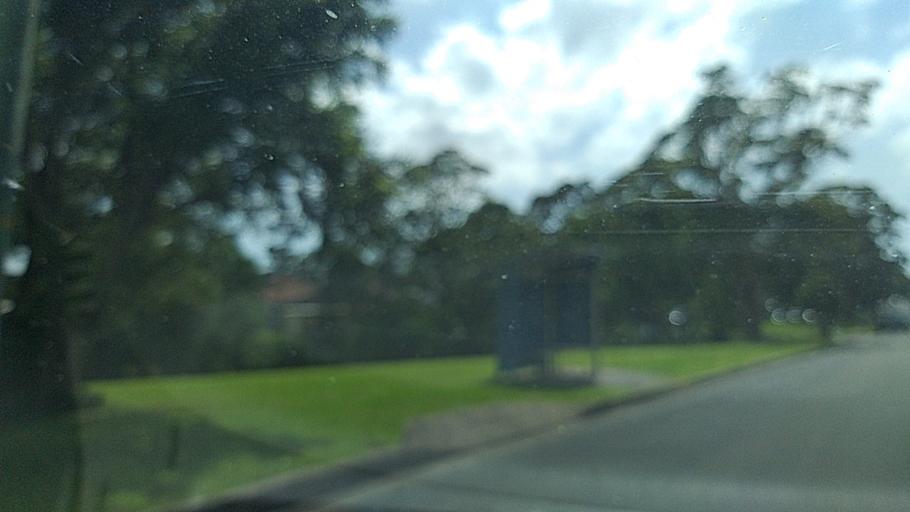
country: AU
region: New South Wales
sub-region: Wollongong
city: Corrimal
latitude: -34.3745
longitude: 150.8942
